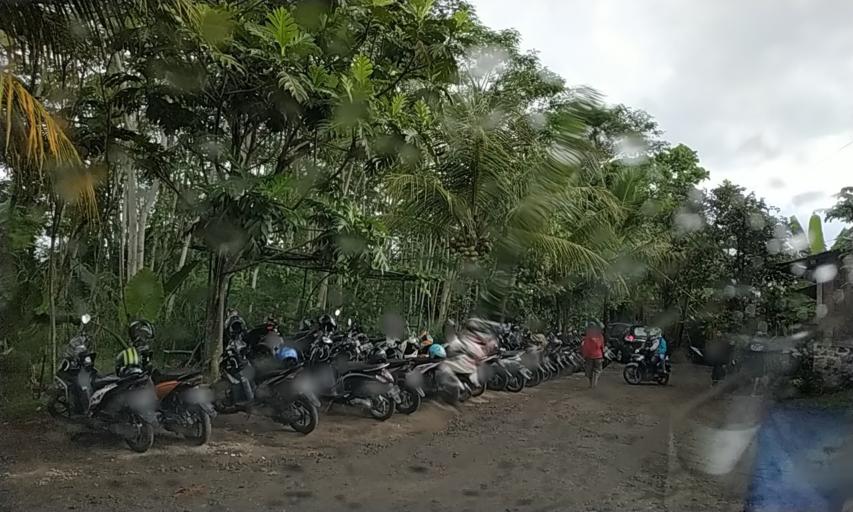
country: ID
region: Daerah Istimewa Yogyakarta
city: Sleman
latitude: -7.6706
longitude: 110.4215
